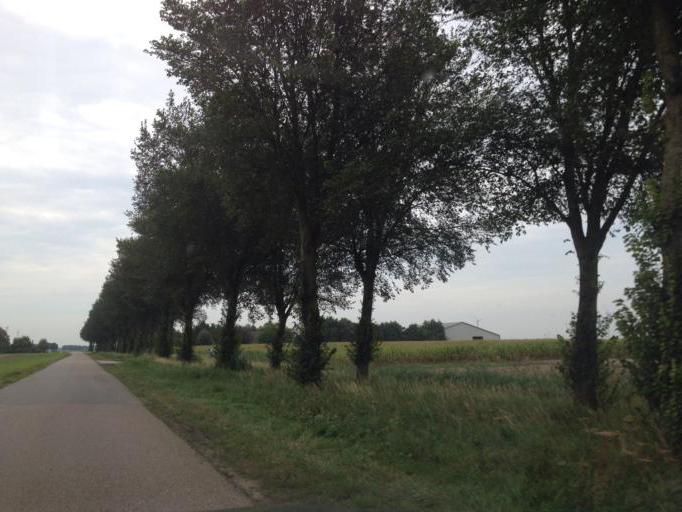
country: NL
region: Utrecht
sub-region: Gemeente Bunschoten
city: Spakenburg
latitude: 52.3603
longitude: 5.3567
